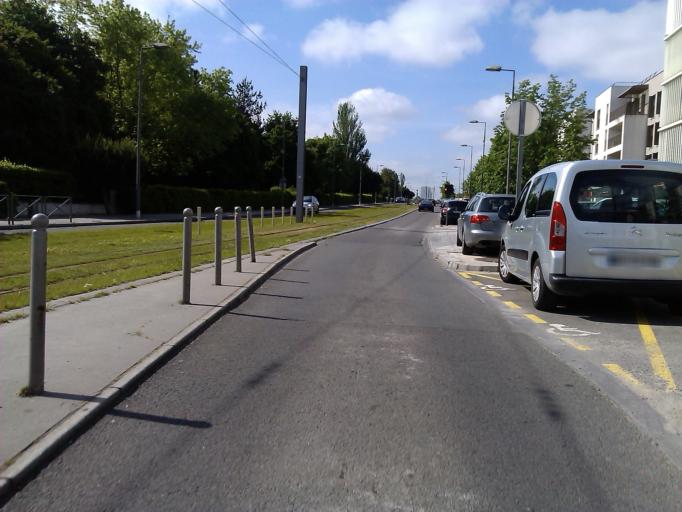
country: FR
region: Aquitaine
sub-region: Departement de la Gironde
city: Lormont
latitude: 44.8758
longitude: -0.5195
